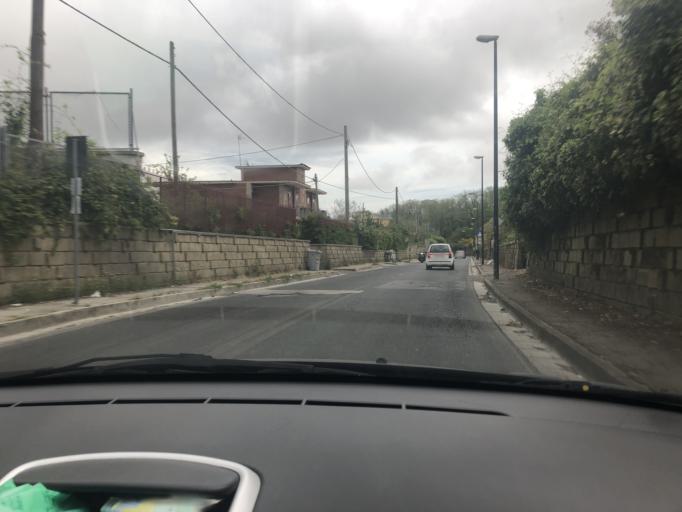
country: IT
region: Campania
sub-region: Provincia di Napoli
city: Torre Caracciolo
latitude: 40.8639
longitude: 14.1984
